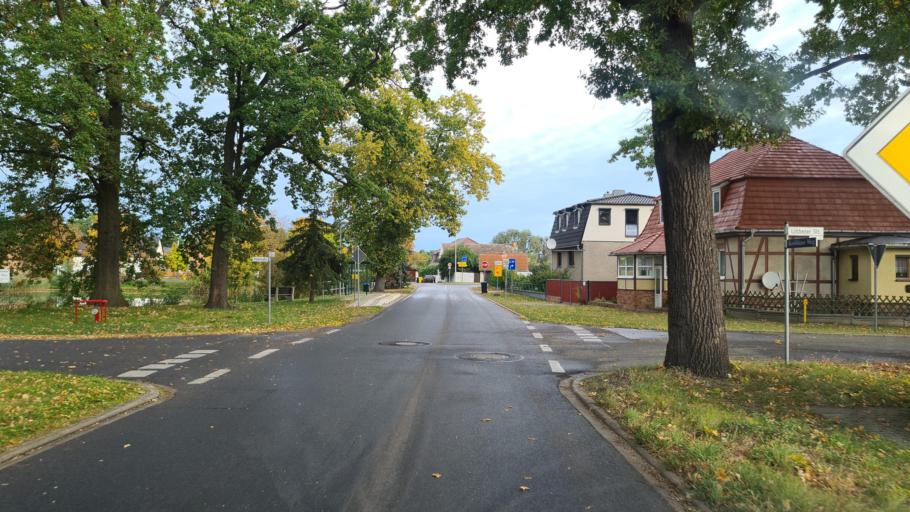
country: DE
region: Brandenburg
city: Kasel-Golzig
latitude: 51.9341
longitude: 13.7062
